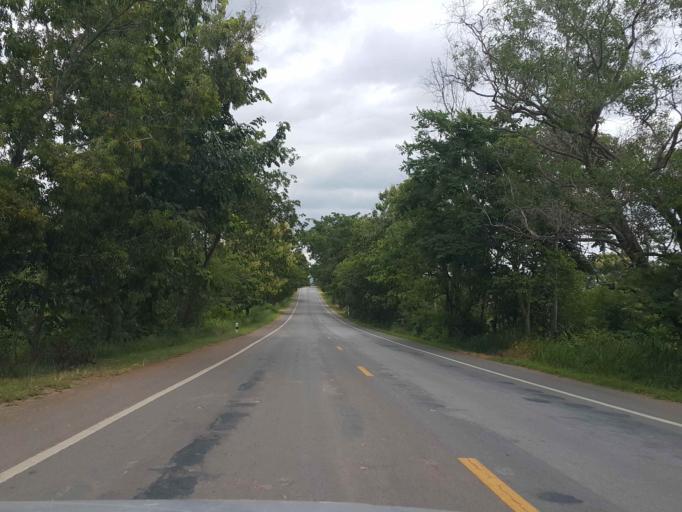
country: TH
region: Lamphun
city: Thung Hua Chang
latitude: 17.9761
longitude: 98.8766
